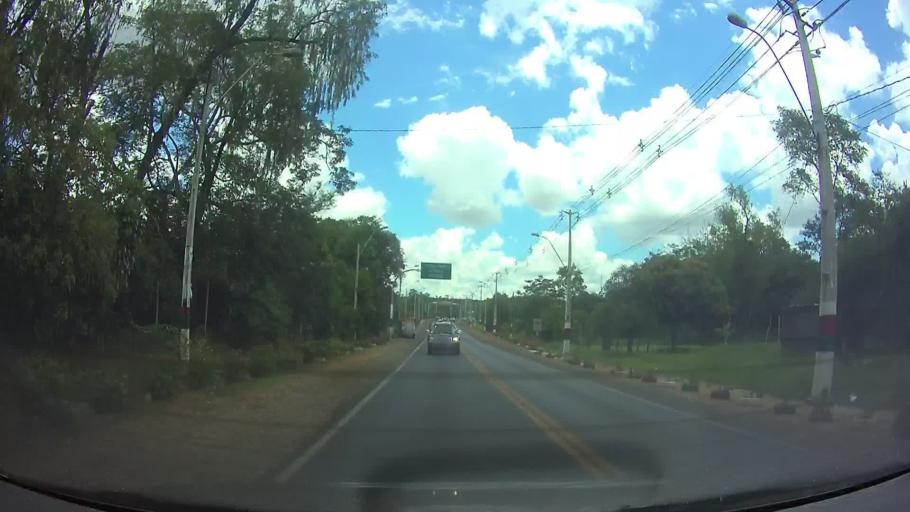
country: PY
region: Central
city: Aregua
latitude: -25.2928
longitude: -57.4428
